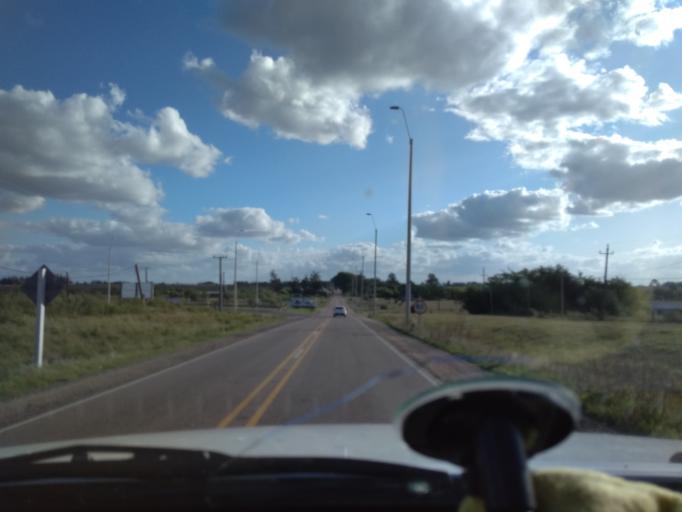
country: UY
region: Canelones
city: Tala
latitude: -34.3618
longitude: -55.7762
